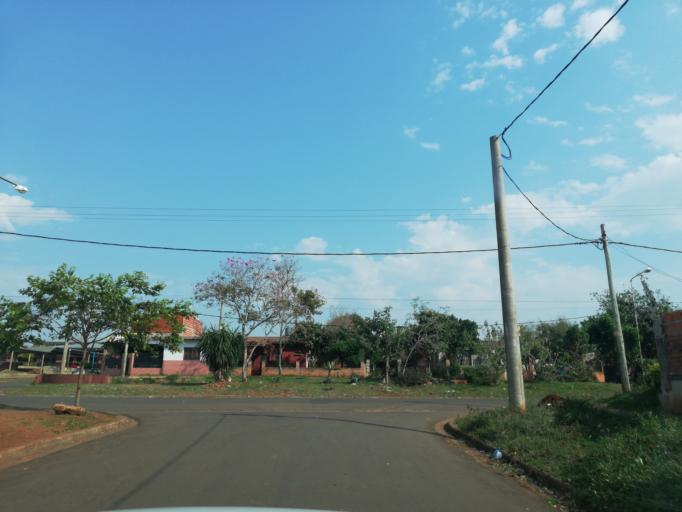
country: AR
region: Misiones
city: Garupa
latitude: -27.4338
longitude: -55.8755
